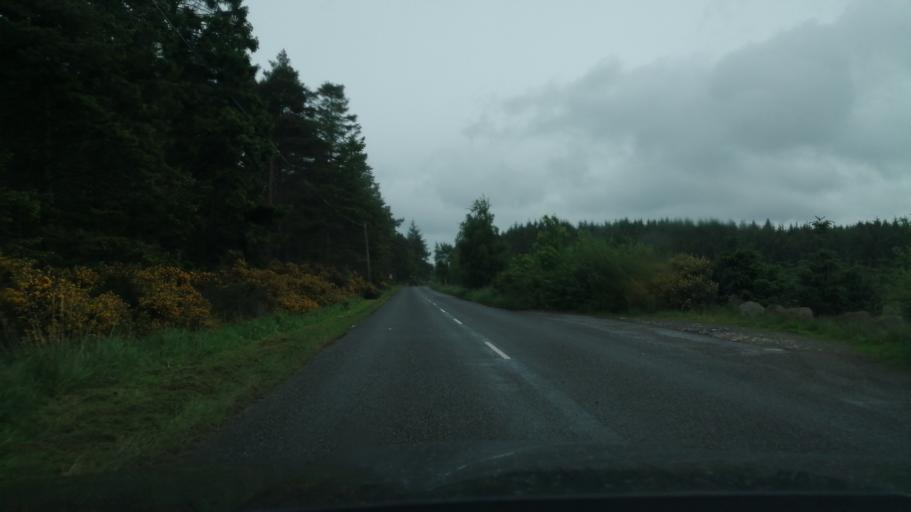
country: GB
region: Scotland
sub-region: Aberdeenshire
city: Portsoy
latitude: 57.6247
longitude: -2.7206
